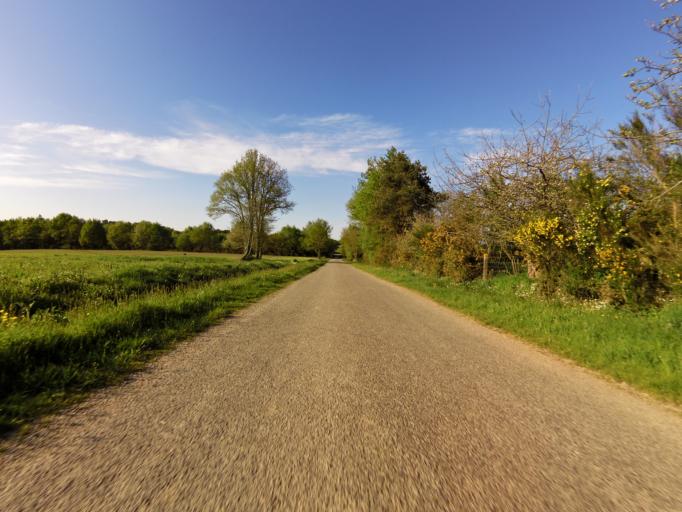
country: FR
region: Brittany
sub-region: Departement du Morbihan
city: Molac
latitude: 47.7403
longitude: -2.4760
